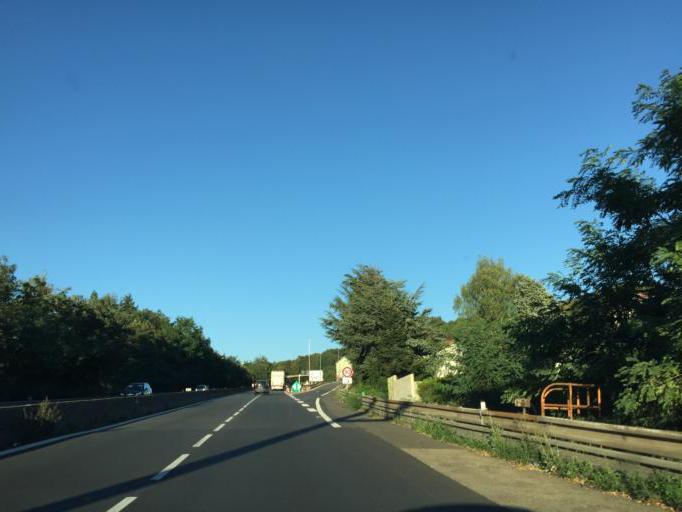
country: FR
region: Rhone-Alpes
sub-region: Departement de la Loire
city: Le Chambon-Feugerolles
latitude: 45.3965
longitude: 4.3488
